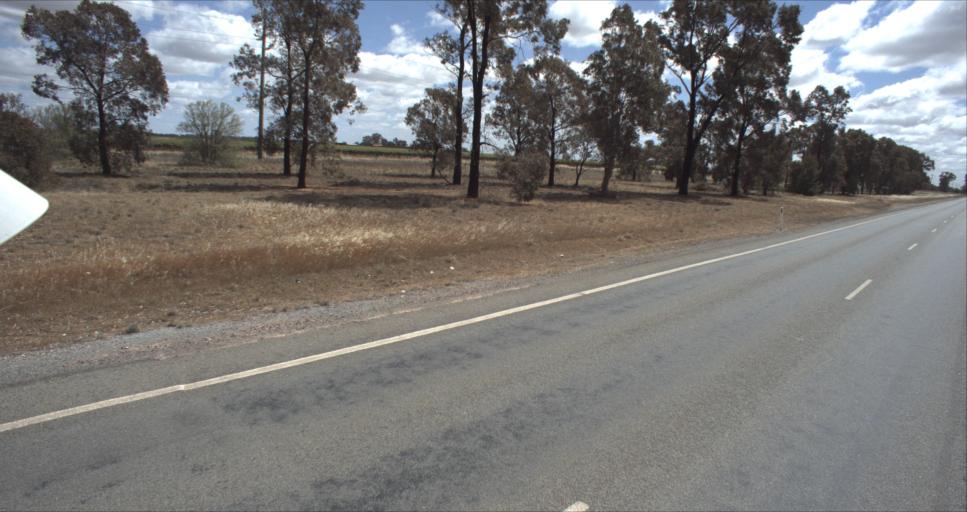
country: AU
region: New South Wales
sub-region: Murrumbidgee Shire
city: Darlington Point
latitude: -34.5088
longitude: 146.1867
